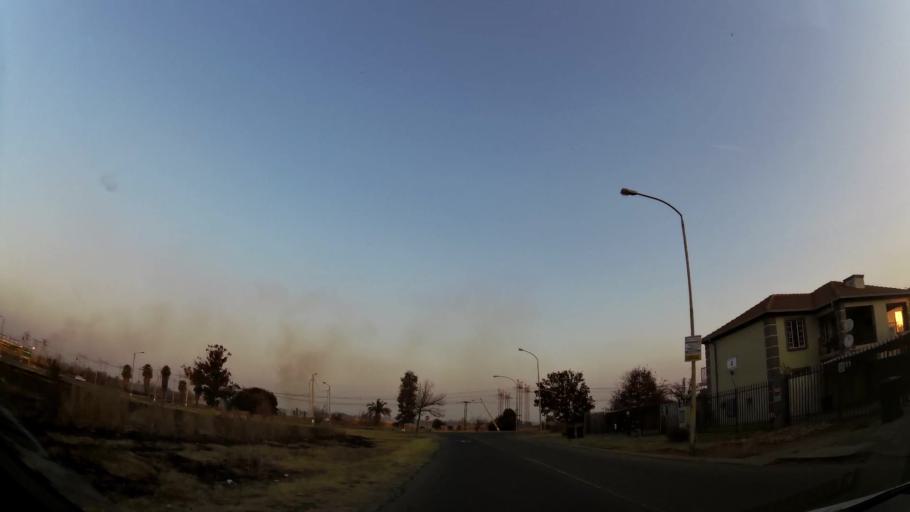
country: ZA
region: Gauteng
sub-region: Ekurhuleni Metropolitan Municipality
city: Springs
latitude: -26.3159
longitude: 28.4543
